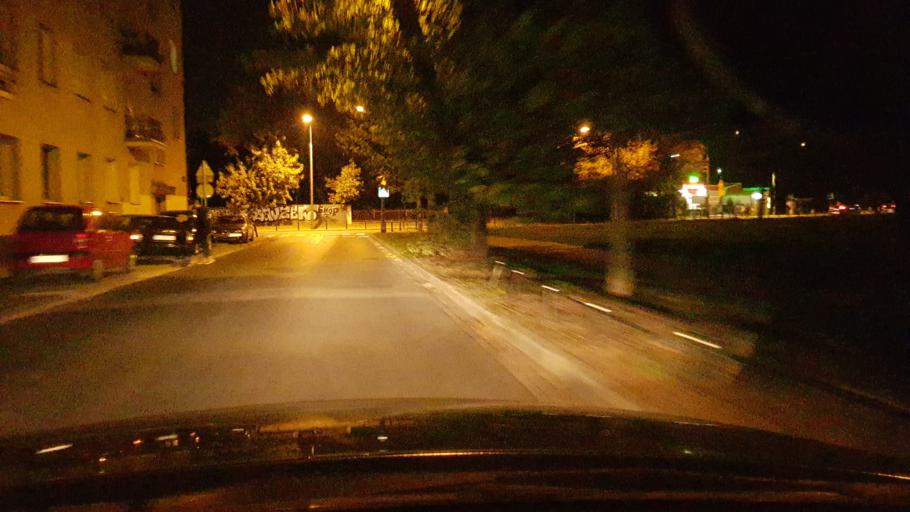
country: PL
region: Masovian Voivodeship
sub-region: Warszawa
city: Praga Polnoc
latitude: 52.2694
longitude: 21.0418
